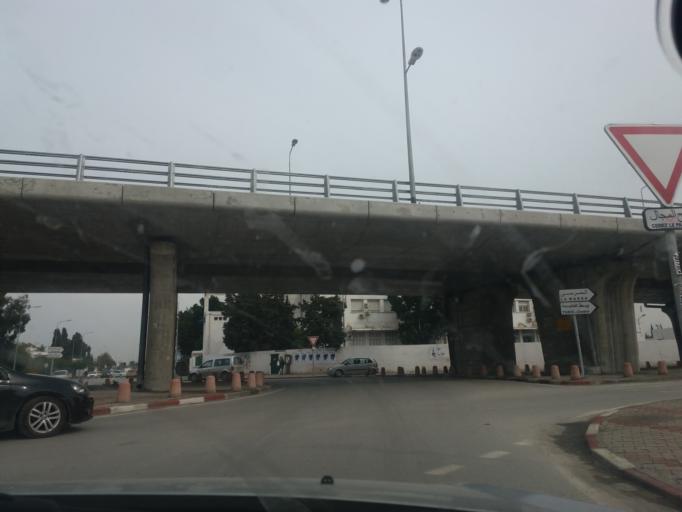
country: TN
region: Tunis
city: Tunis
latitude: 36.8327
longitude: 10.1802
